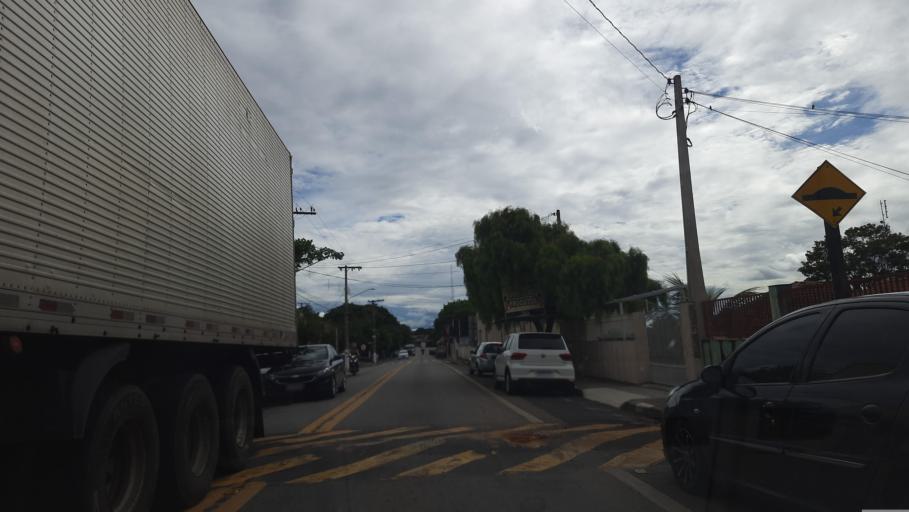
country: BR
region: Sao Paulo
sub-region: Sao Joao Da Boa Vista
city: Sao Joao da Boa Vista
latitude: -21.9466
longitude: -46.7180
